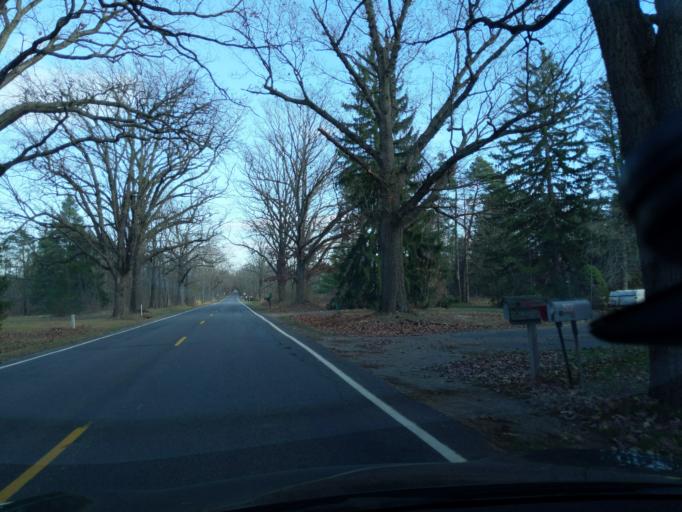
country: US
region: Michigan
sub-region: Ingham County
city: Haslett
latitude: 42.7154
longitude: -84.3528
